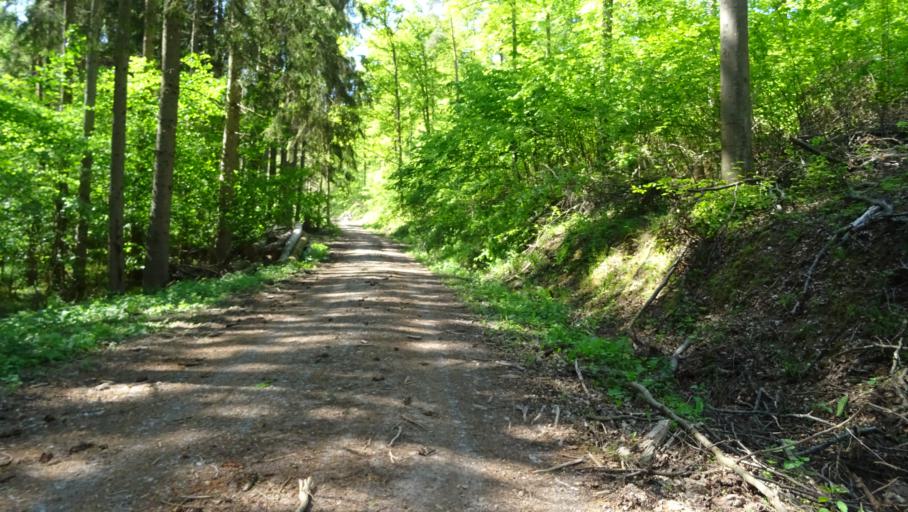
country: DE
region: Baden-Wuerttemberg
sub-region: Karlsruhe Region
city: Limbach
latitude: 49.4132
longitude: 9.2341
